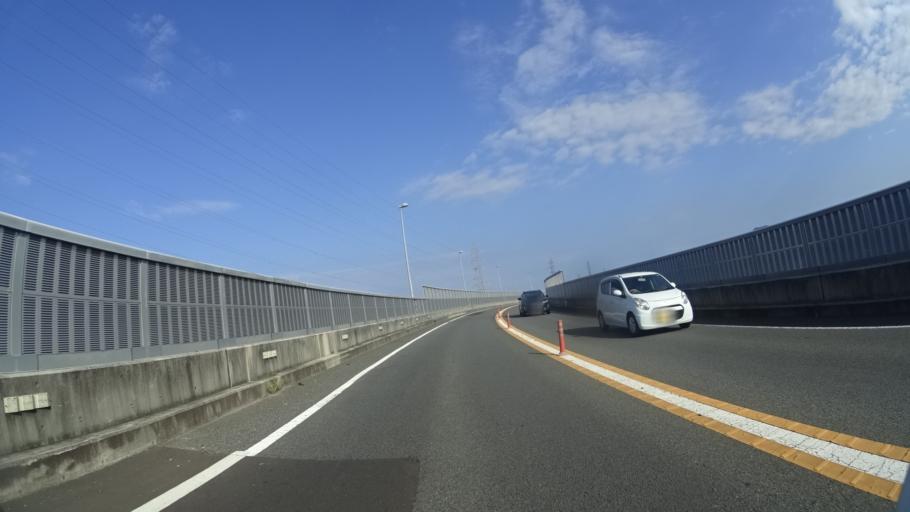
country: JP
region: Shimane
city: Izumo
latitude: 35.3255
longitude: 132.7056
